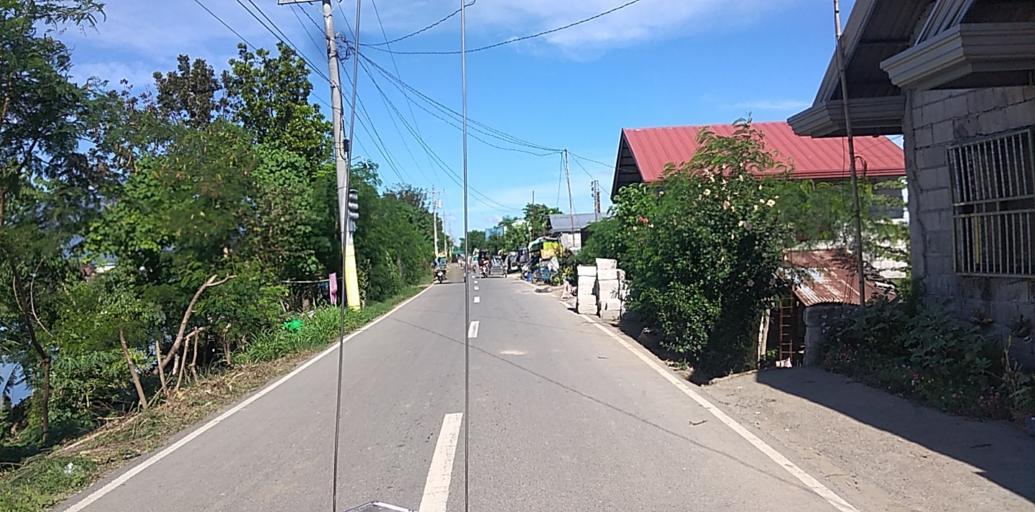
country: PH
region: Central Luzon
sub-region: Province of Pampanga
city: Candaba
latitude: 15.1103
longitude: 120.8166
